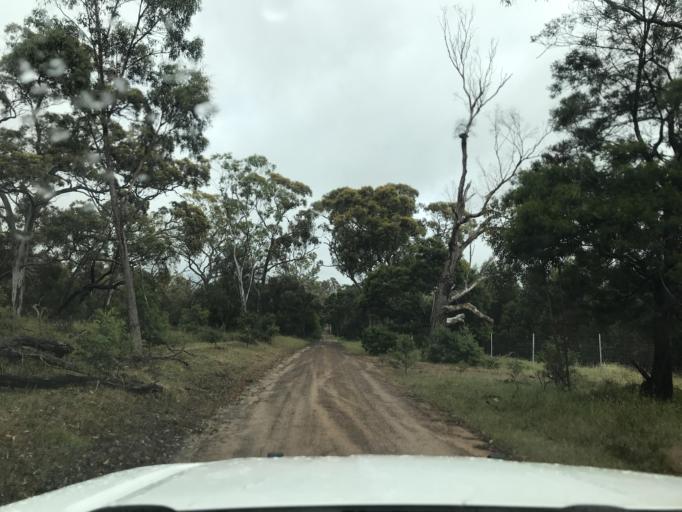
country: AU
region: South Australia
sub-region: Wattle Range
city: Penola
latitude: -37.2647
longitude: 141.3145
